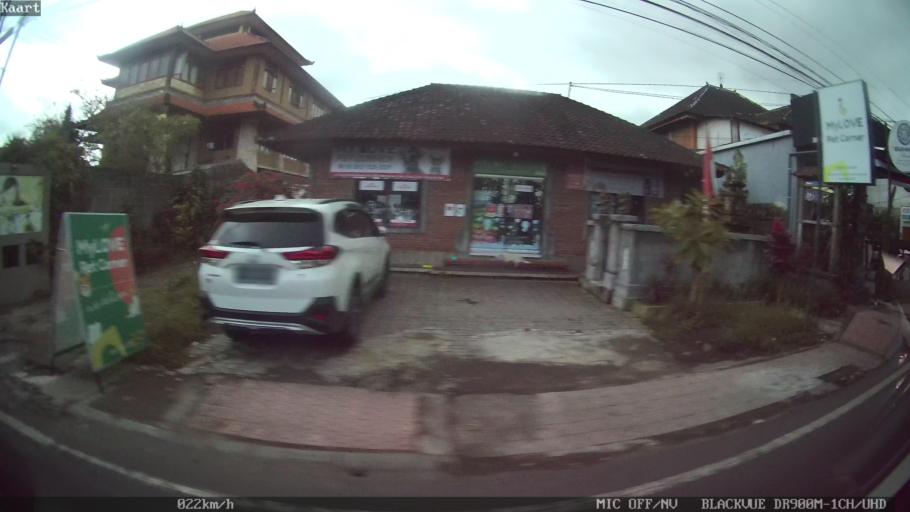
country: ID
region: Bali
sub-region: Kabupaten Gianyar
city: Ubud
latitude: -8.4973
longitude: 115.2534
